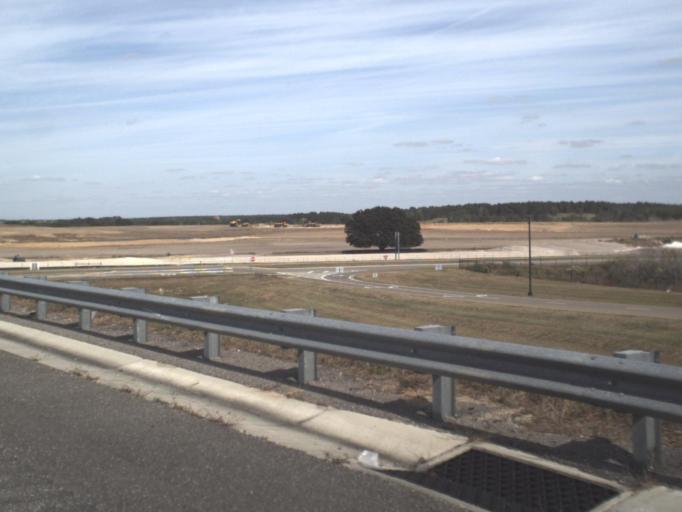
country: US
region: Florida
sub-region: Polk County
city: Citrus Ridge
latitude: 28.4181
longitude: -81.6313
